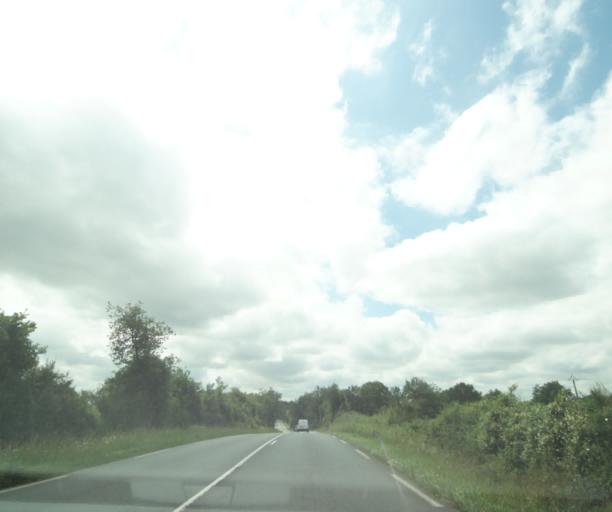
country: FR
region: Poitou-Charentes
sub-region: Departement des Deux-Sevres
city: Viennay
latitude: 46.7139
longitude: -0.2394
